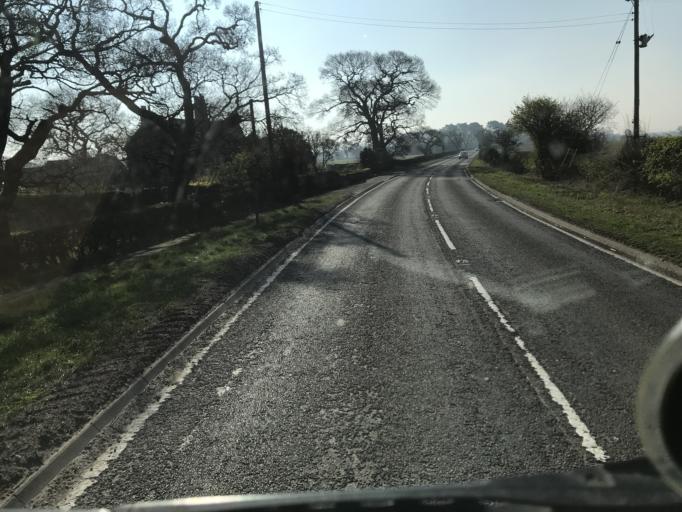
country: GB
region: England
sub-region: Cheshire West and Chester
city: Waverton
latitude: 53.1606
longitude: -2.8148
